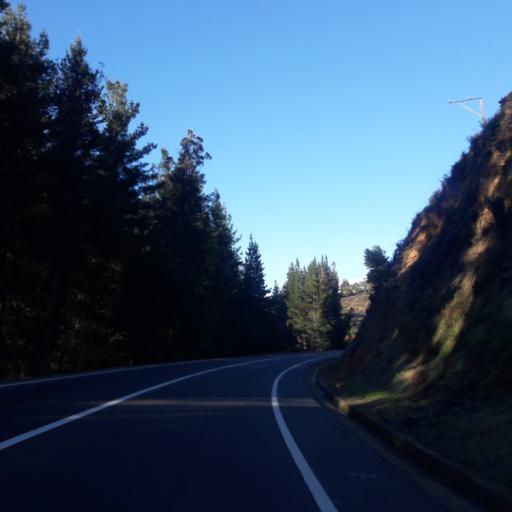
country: CL
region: Biobio
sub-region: Provincia de Concepcion
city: Lota
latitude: -37.2475
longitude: -72.9619
